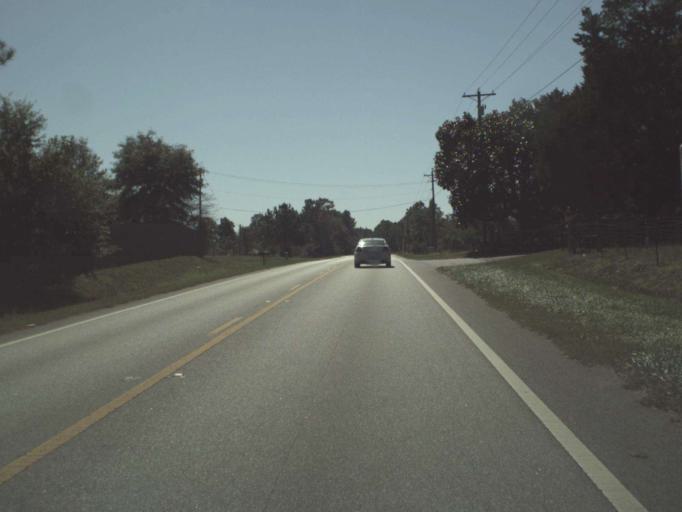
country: US
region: Florida
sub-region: Walton County
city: DeFuniak Springs
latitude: 30.7973
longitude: -86.1223
